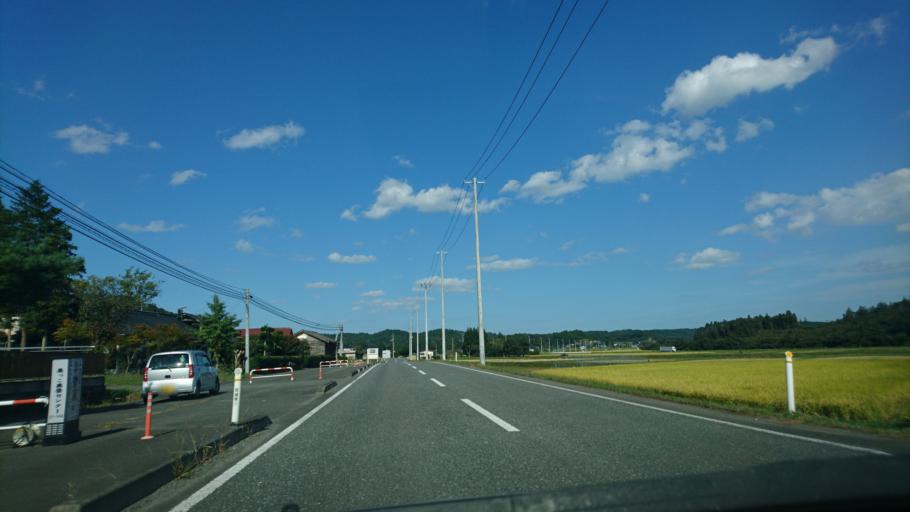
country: JP
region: Iwate
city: Ichinoseki
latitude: 38.8369
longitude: 141.0137
